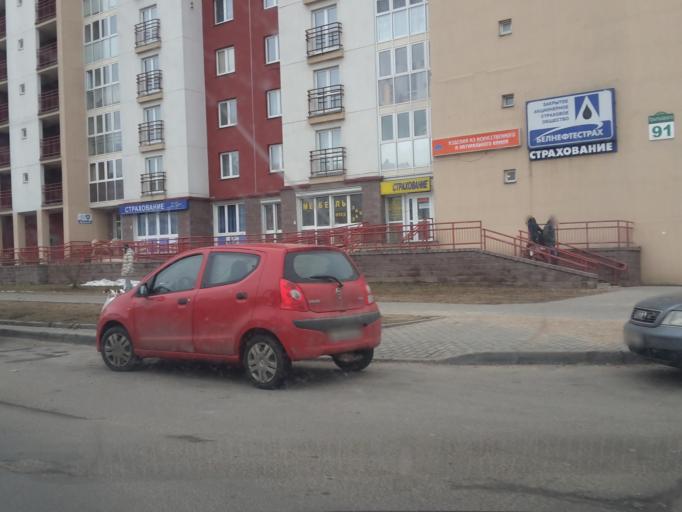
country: BY
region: Minsk
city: Novoye Medvezhino
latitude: 53.9064
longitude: 27.4418
